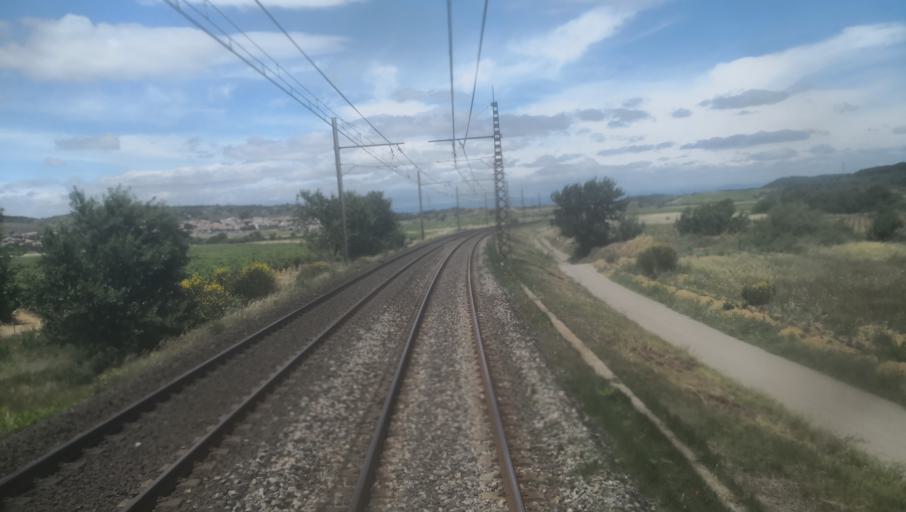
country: FR
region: Languedoc-Roussillon
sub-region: Departement de l'Aude
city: Marcorignan
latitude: 43.1870
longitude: 2.9397
